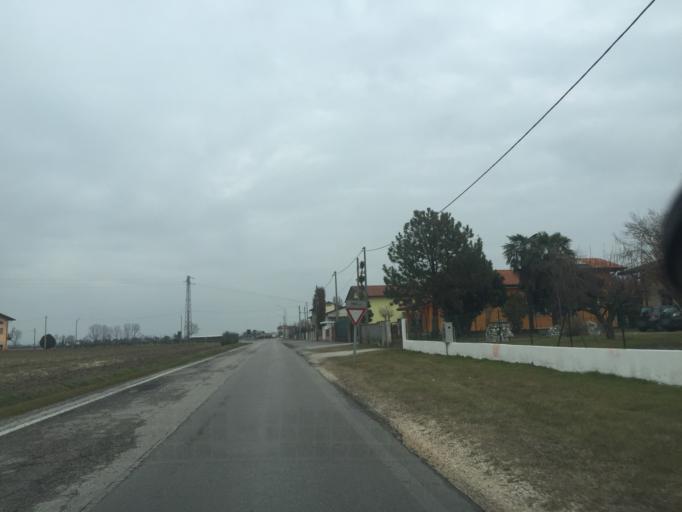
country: IT
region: Friuli Venezia Giulia
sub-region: Provincia di Pordenone
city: Cavolano-Schiavoi
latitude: 45.9380
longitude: 12.5207
